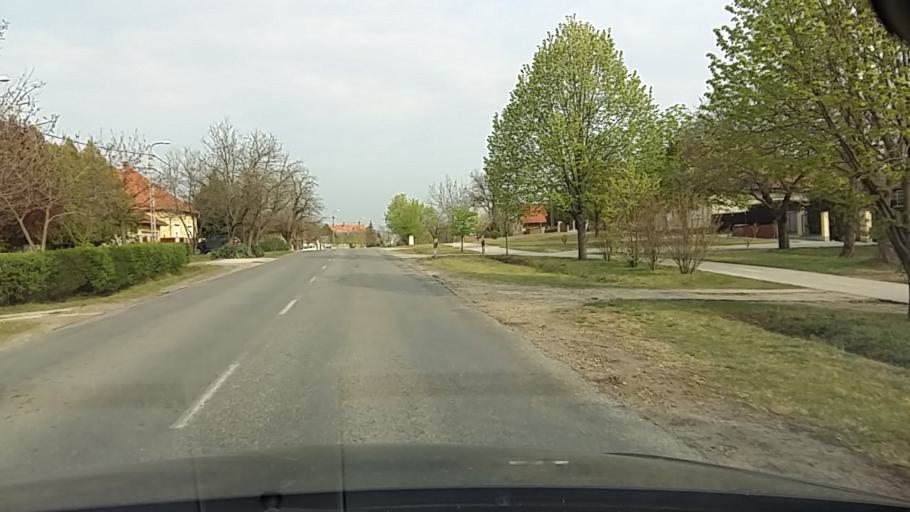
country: HU
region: Pest
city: Taksony
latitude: 47.3229
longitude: 19.0679
